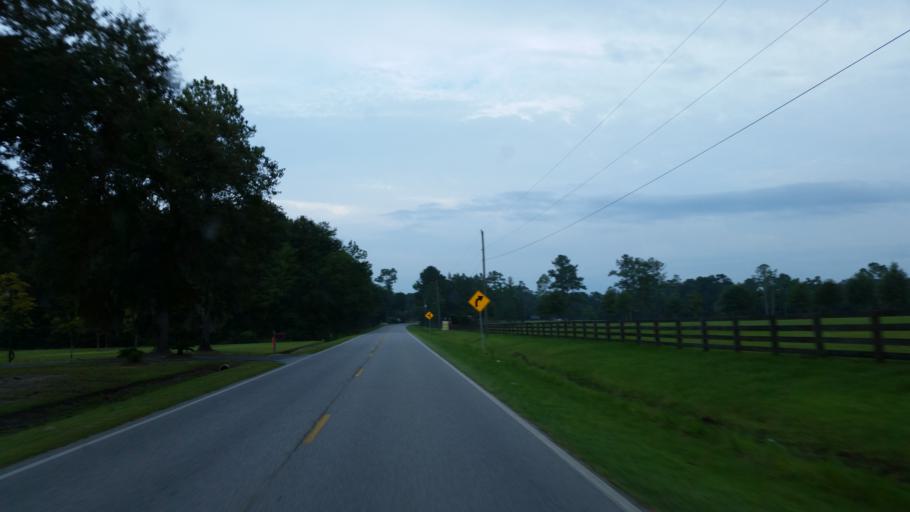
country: US
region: Georgia
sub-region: Lowndes County
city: Valdosta
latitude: 30.7607
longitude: -83.2621
